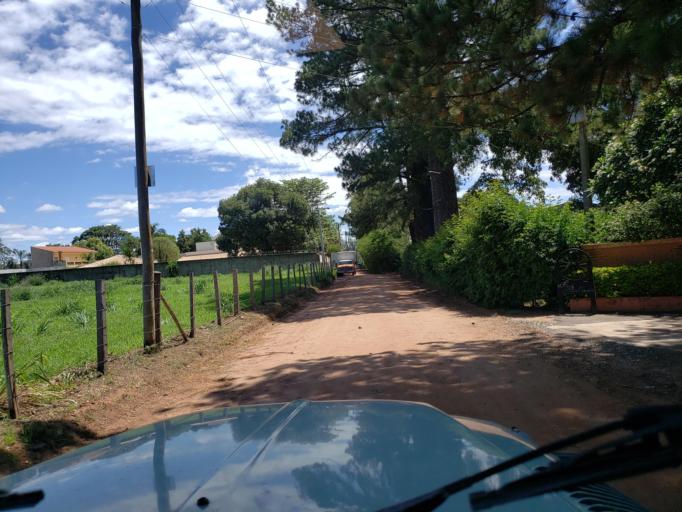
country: BR
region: Sao Paulo
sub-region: Moji-Guacu
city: Mogi-Gaucu
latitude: -22.3039
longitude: -46.9069
